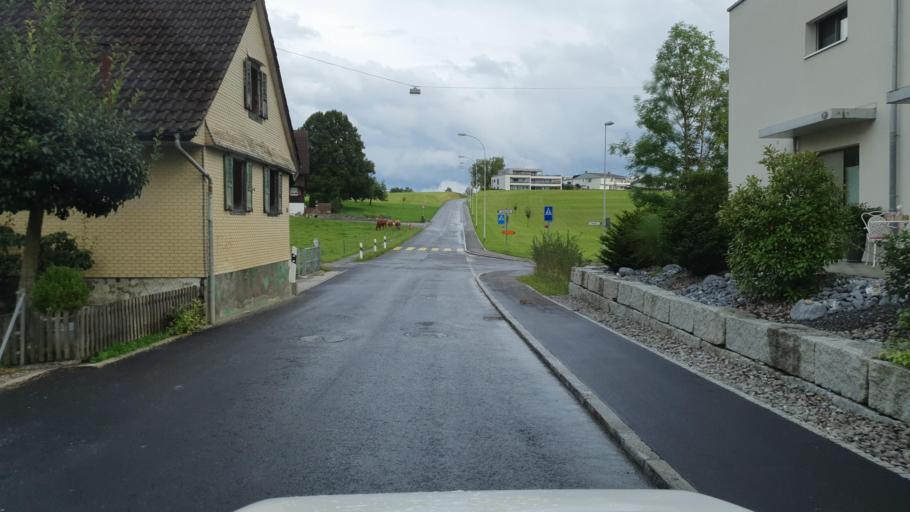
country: CH
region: Lucerne
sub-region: Hochdorf District
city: Ballwil
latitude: 47.1516
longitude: 8.3275
